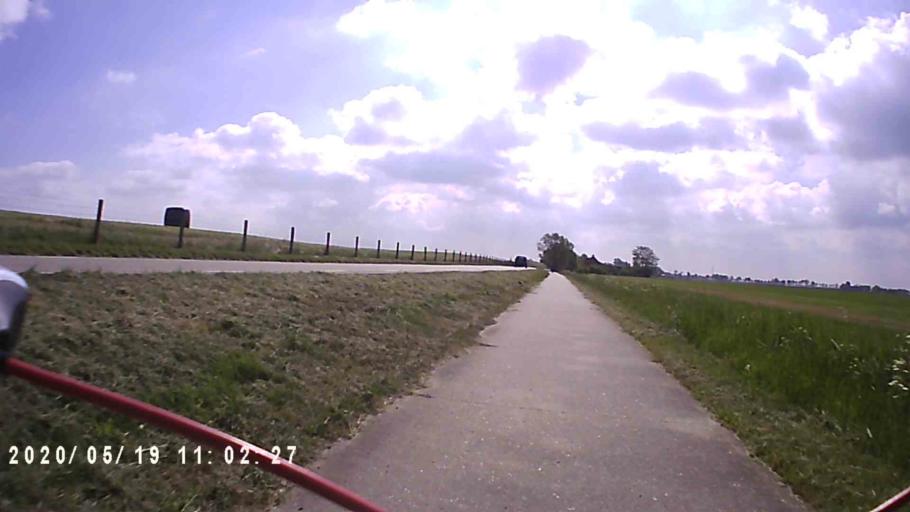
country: NL
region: Groningen
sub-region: Gemeente Zuidhorn
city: Grijpskerk
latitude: 53.3005
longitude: 6.2774
